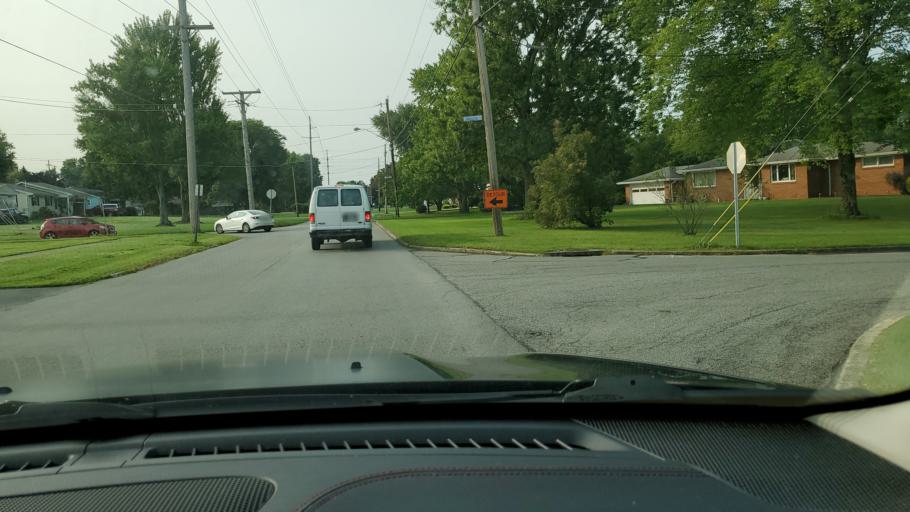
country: US
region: Ohio
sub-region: Mahoning County
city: Poland
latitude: 41.0339
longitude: -80.6212
